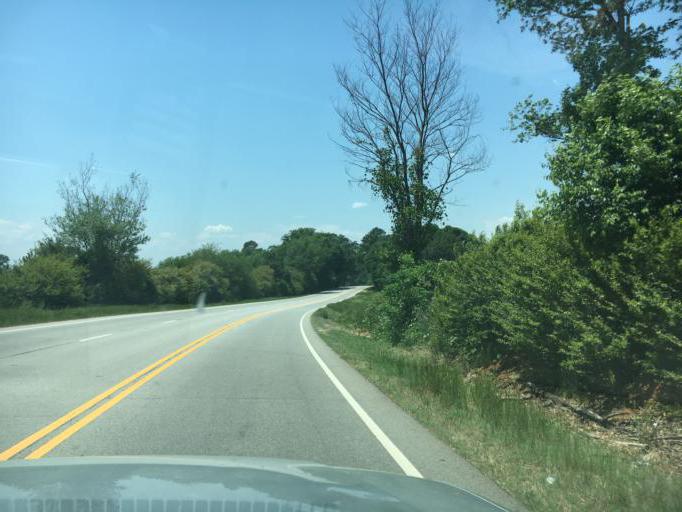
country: US
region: Georgia
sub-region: Hart County
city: Royston
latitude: 34.2880
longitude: -83.0555
